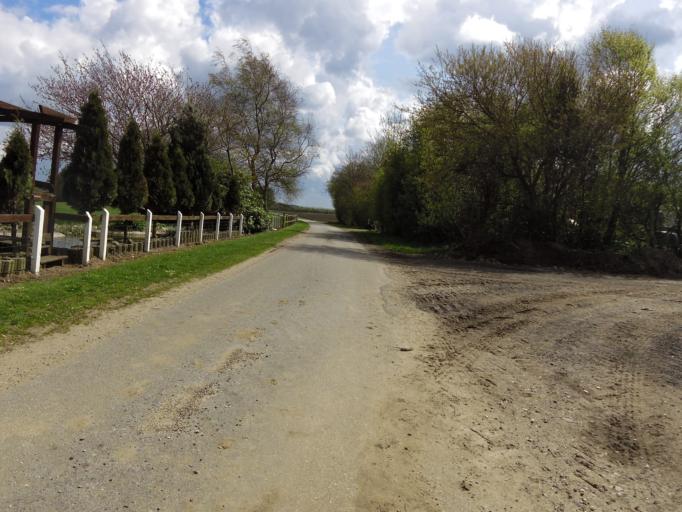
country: DK
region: South Denmark
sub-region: Tonder Kommune
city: Toftlund
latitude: 55.2107
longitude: 9.1565
